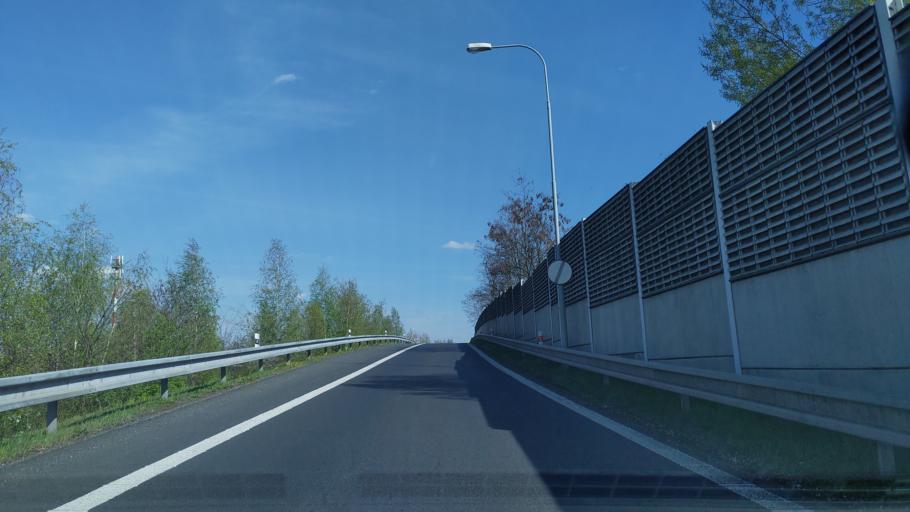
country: CZ
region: Ustecky
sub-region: Okres Most
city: Most
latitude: 50.5264
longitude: 13.6258
